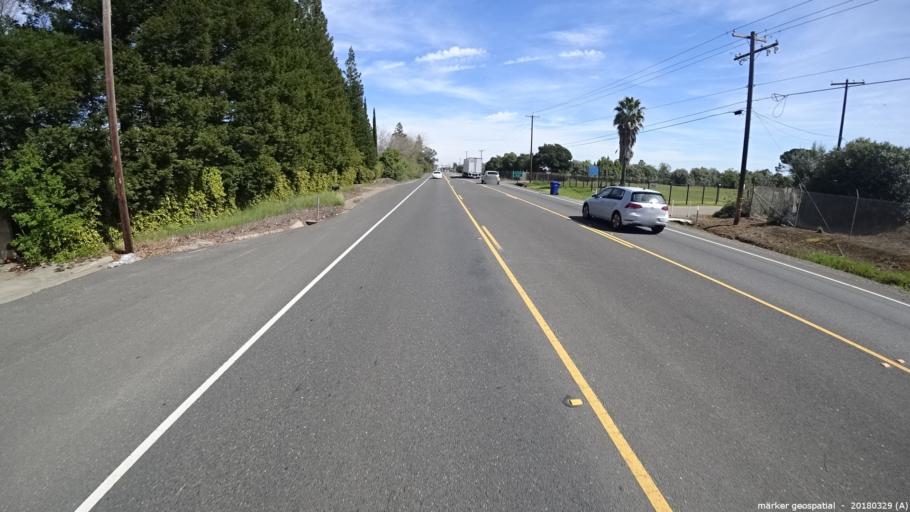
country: US
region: California
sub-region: Sacramento County
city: Rosemont
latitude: 38.5378
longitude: -121.3675
